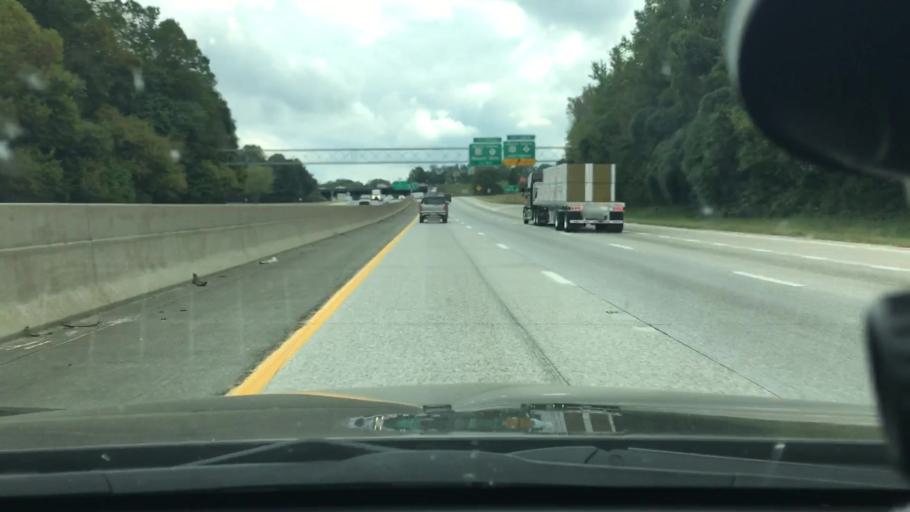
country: US
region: North Carolina
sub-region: Forsyth County
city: Winston-Salem
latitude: 36.0648
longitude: -80.2363
